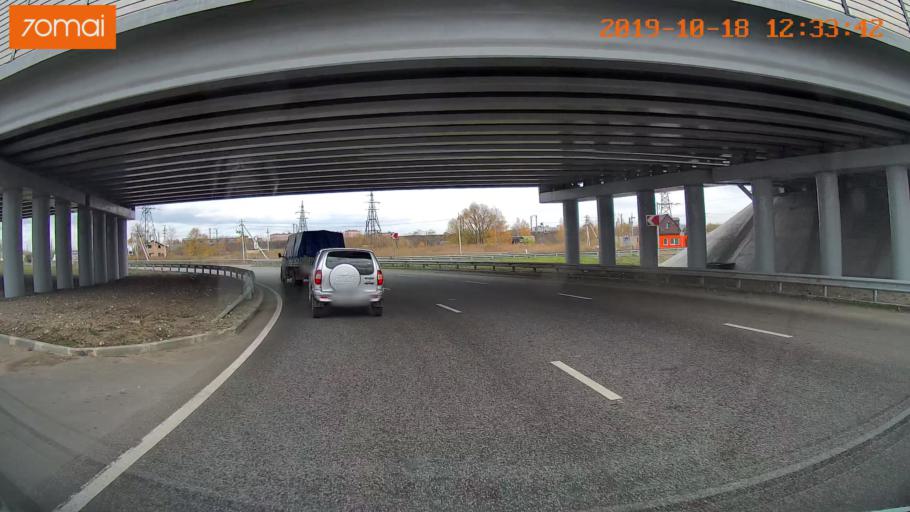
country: RU
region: Rjazan
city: Ryazan'
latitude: 54.6093
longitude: 39.6401
